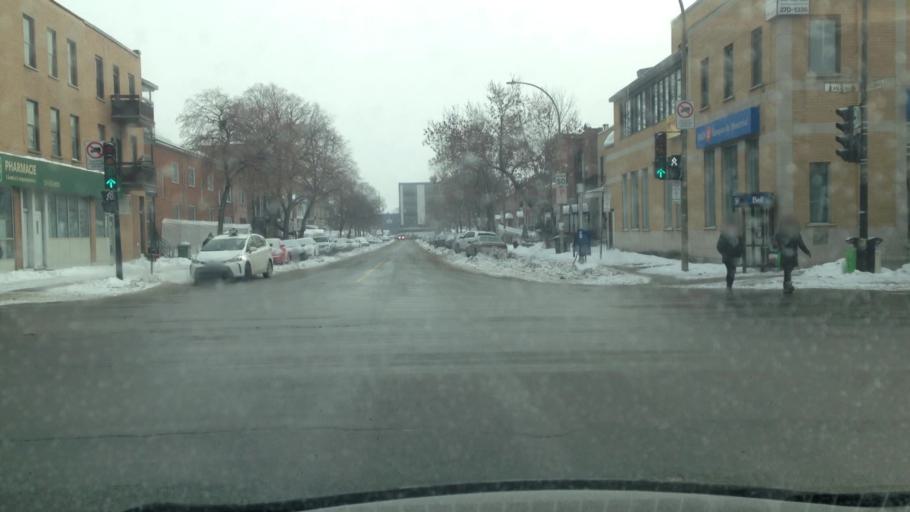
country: CA
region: Quebec
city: Mont-Royal
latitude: 45.5285
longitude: -73.6235
